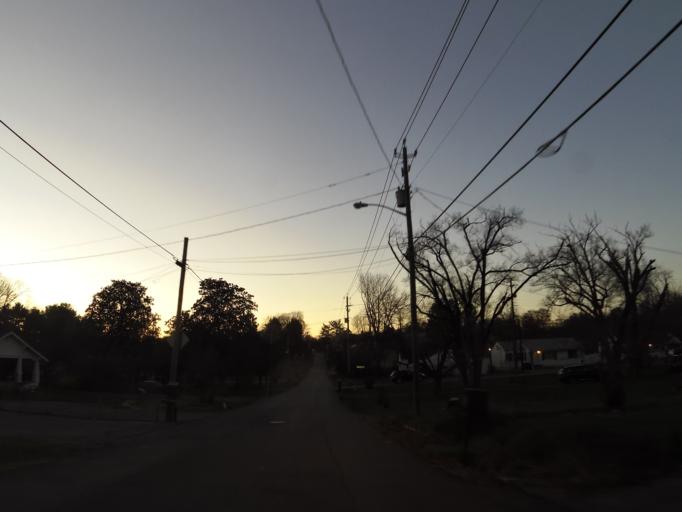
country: US
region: Tennessee
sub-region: Knox County
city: Knoxville
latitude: 36.0150
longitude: -83.9630
